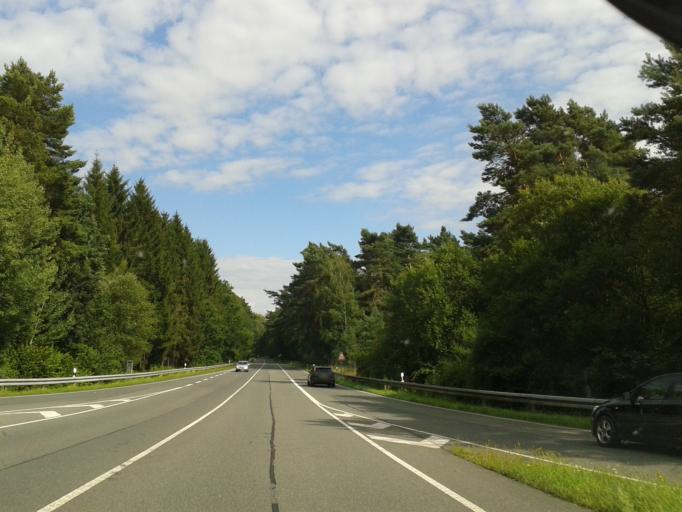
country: DE
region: North Rhine-Westphalia
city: Bad Lippspringe
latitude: 51.8014
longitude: 8.8093
